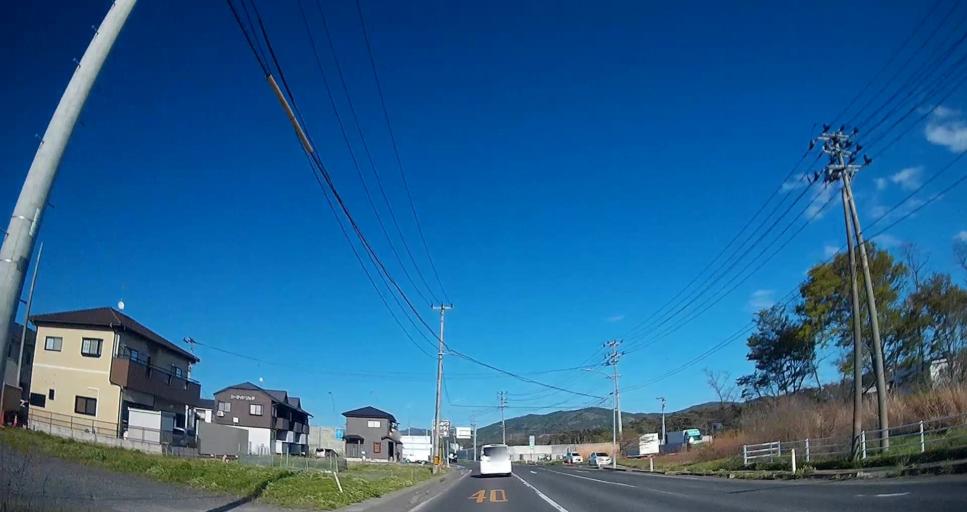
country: JP
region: Miyagi
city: Ishinomaki
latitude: 38.4173
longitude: 141.3462
